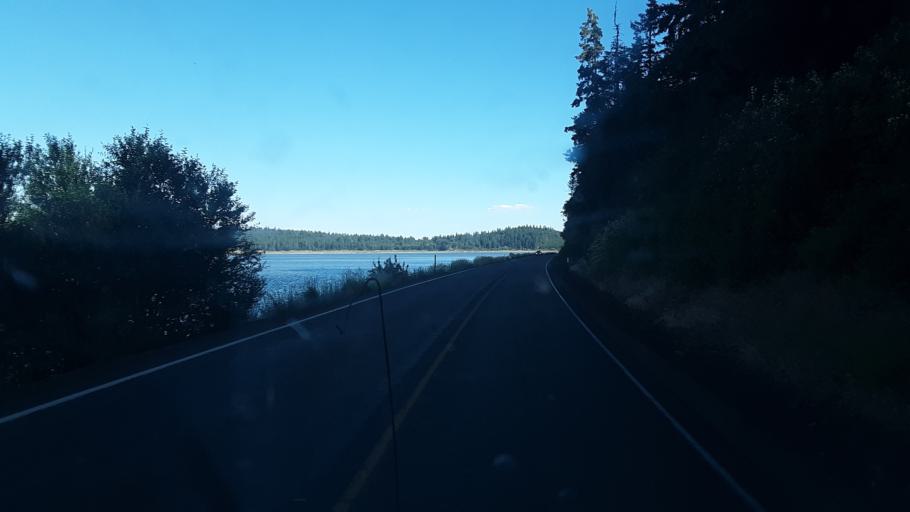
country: US
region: Oregon
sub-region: Klamath County
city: Klamath Falls
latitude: 42.3041
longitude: -121.9358
